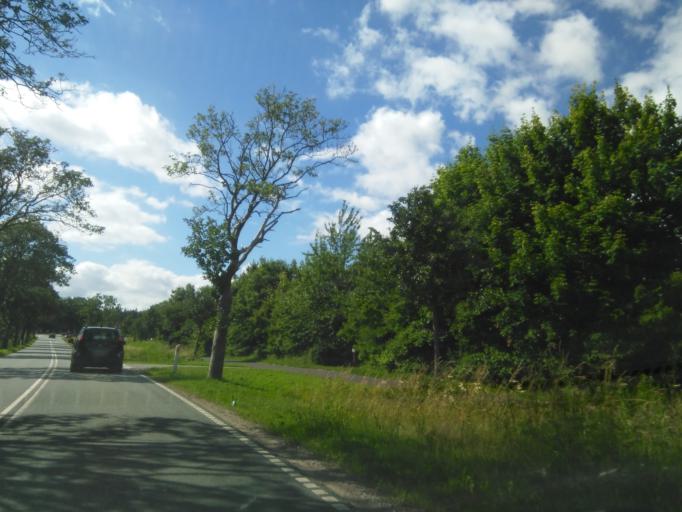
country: DK
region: Central Jutland
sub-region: Syddjurs Kommune
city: Ronde
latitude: 56.2830
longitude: 10.4842
